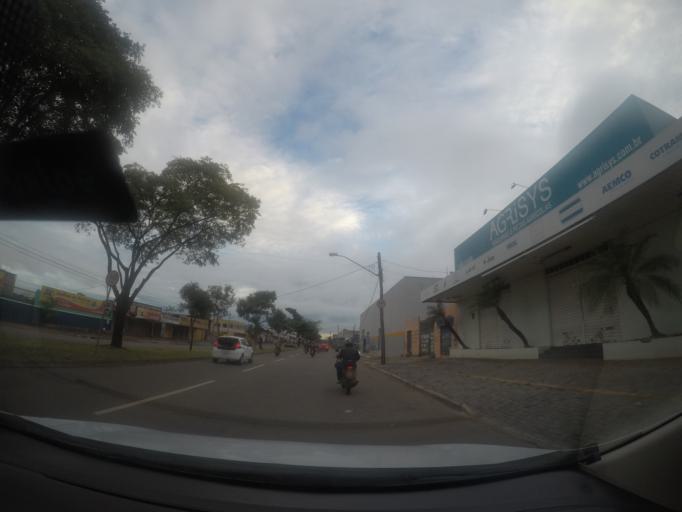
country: BR
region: Goias
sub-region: Goiania
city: Goiania
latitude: -16.6749
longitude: -49.3167
